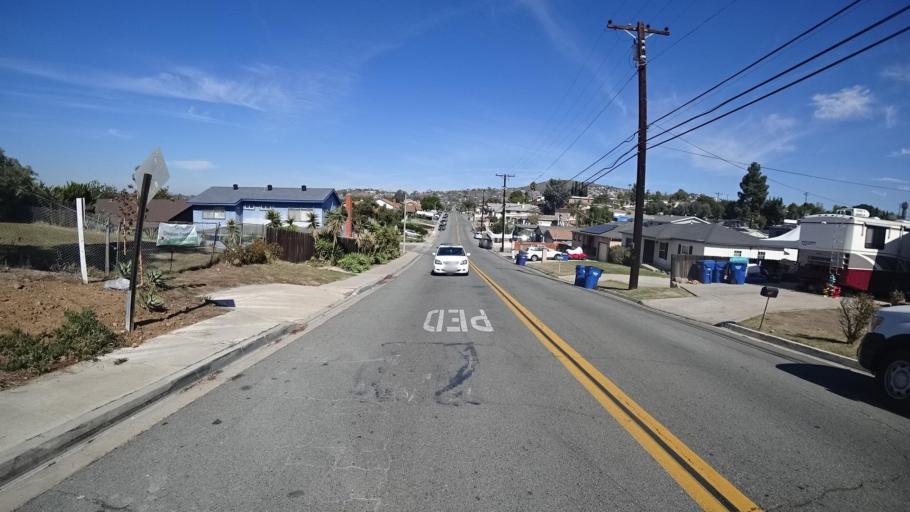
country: US
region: California
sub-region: San Diego County
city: La Presa
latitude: 32.7050
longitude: -117.0020
